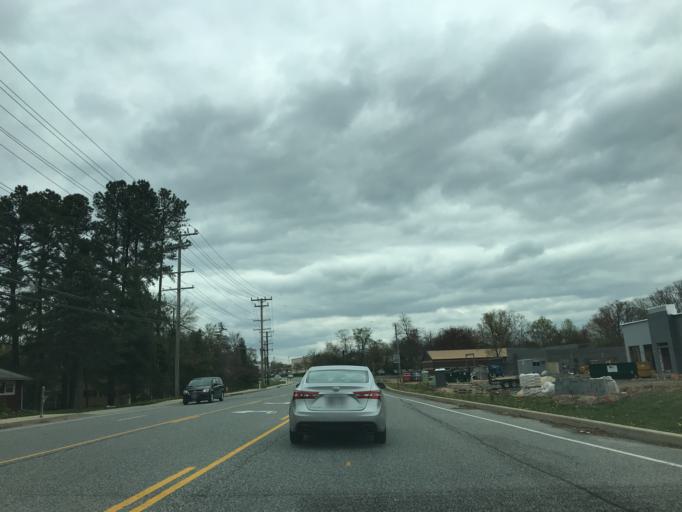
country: US
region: Maryland
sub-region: Harford County
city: Bel Air South
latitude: 39.4704
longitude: -76.3094
